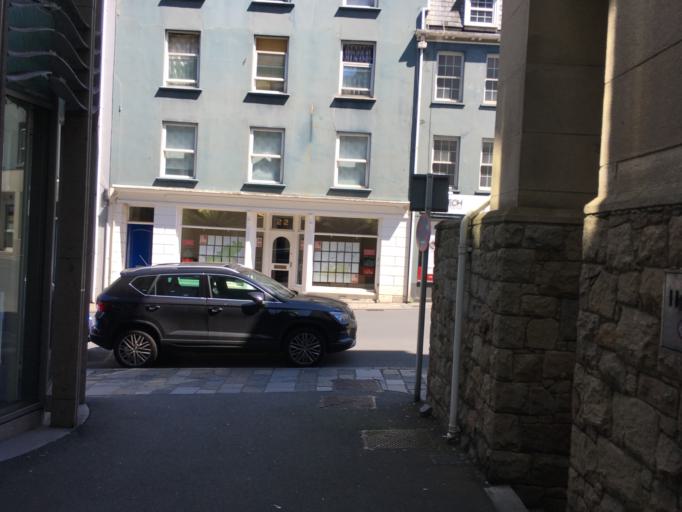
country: GG
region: St Peter Port
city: Saint Peter Port
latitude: 49.4530
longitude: -2.5384
